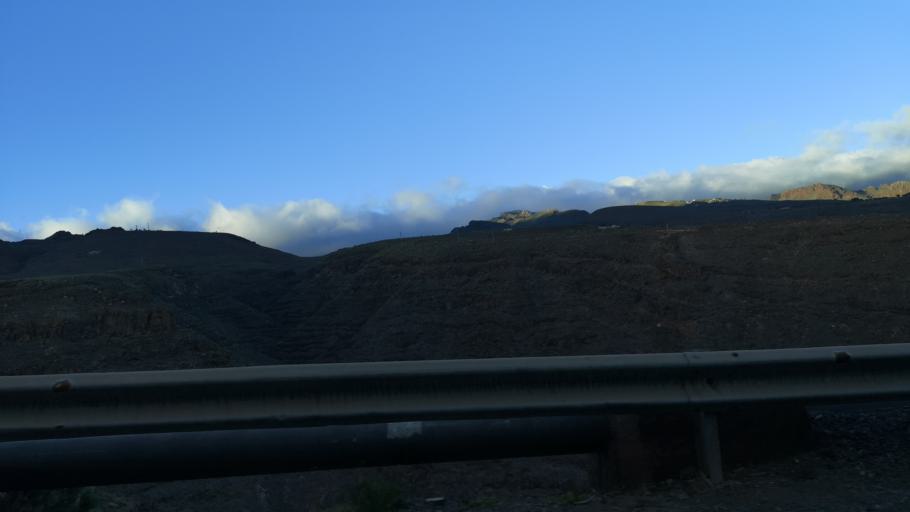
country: ES
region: Canary Islands
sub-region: Provincia de Santa Cruz de Tenerife
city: Alajero
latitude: 28.0331
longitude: -17.2103
